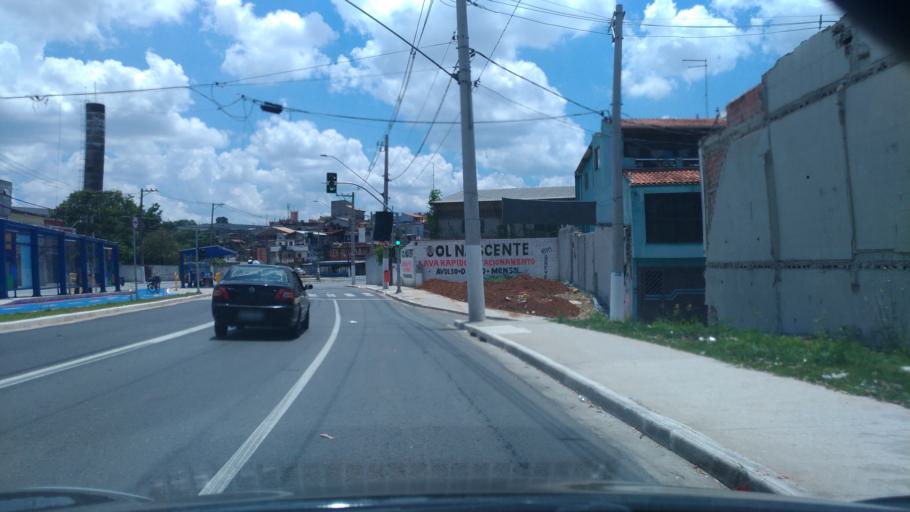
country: BR
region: Sao Paulo
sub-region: Sao Bernardo Do Campo
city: Sao Bernardo do Campo
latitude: -23.7354
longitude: -46.5863
